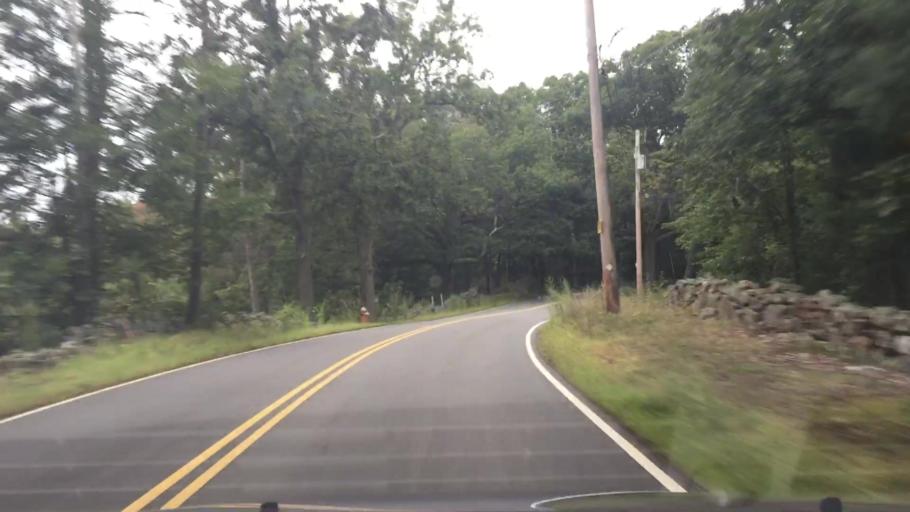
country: US
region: Massachusetts
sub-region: Essex County
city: North Andover
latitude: 42.7059
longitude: -71.0819
